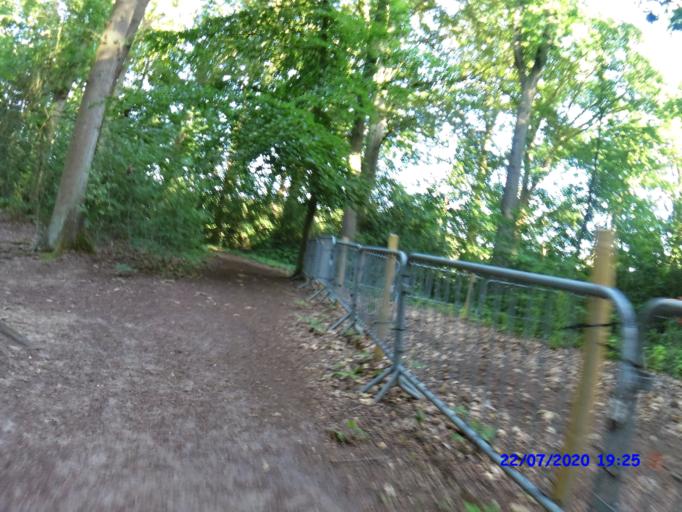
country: BE
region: Flanders
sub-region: Provincie Vlaams-Brabant
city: Aarschot
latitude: 50.9797
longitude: 4.8145
